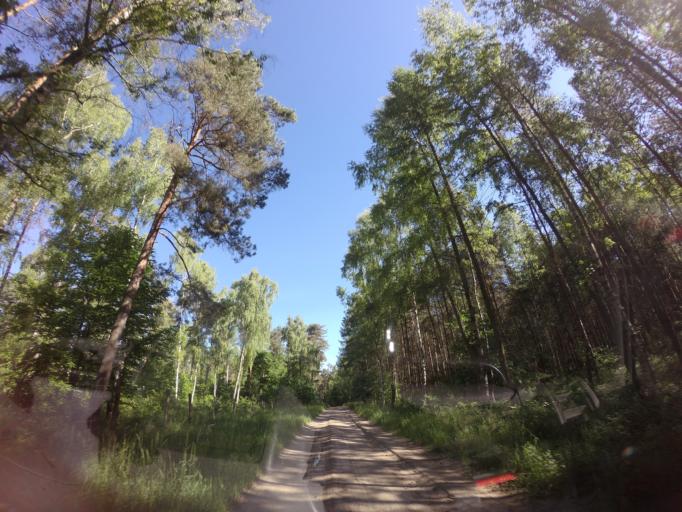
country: PL
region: West Pomeranian Voivodeship
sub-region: Powiat choszczenski
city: Drawno
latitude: 53.2325
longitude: 15.6726
